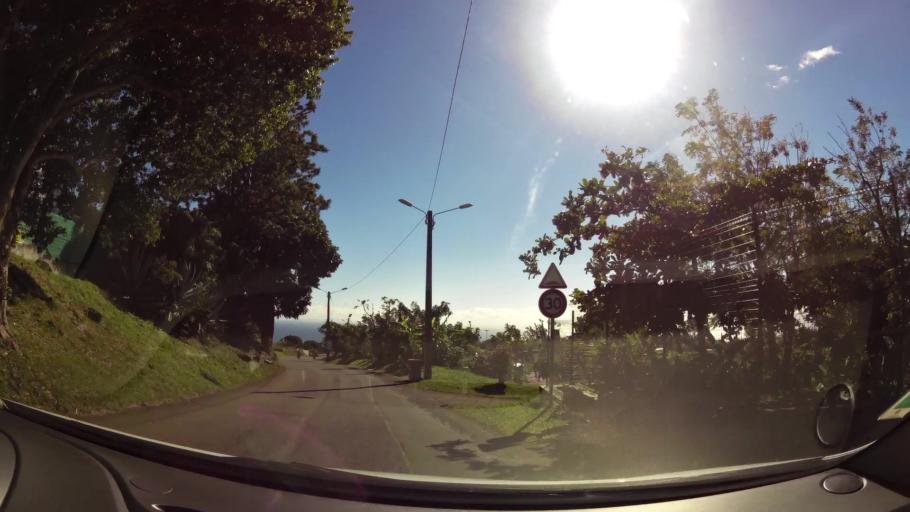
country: RE
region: Reunion
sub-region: Reunion
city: Saint-Denis
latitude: -20.9164
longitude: 55.4783
